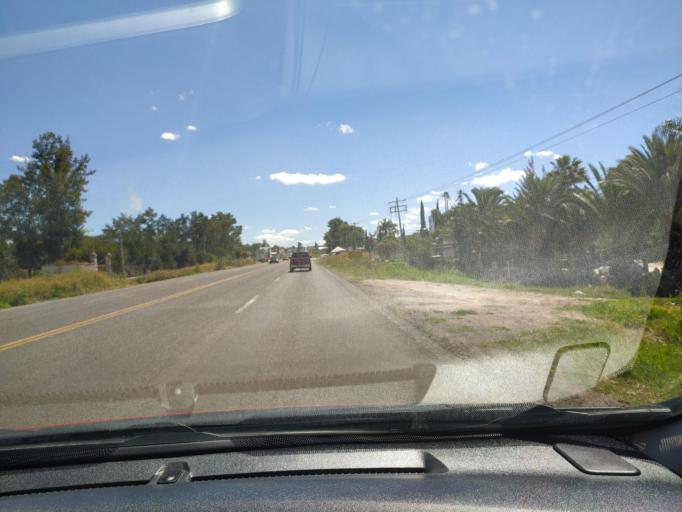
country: MX
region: Jalisco
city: San Miguel el Alto
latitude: 21.0276
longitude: -102.3811
